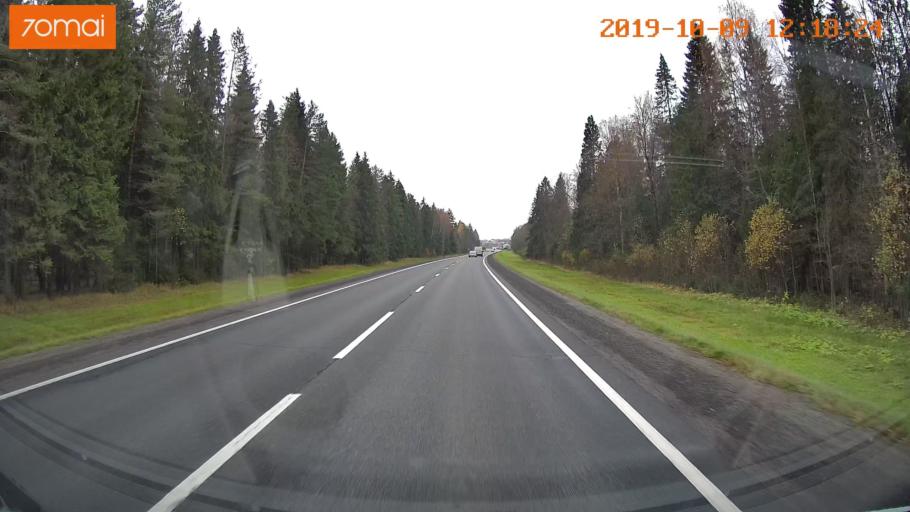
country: RU
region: Jaroslavl
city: Prechistoye
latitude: 58.4428
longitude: 40.3214
